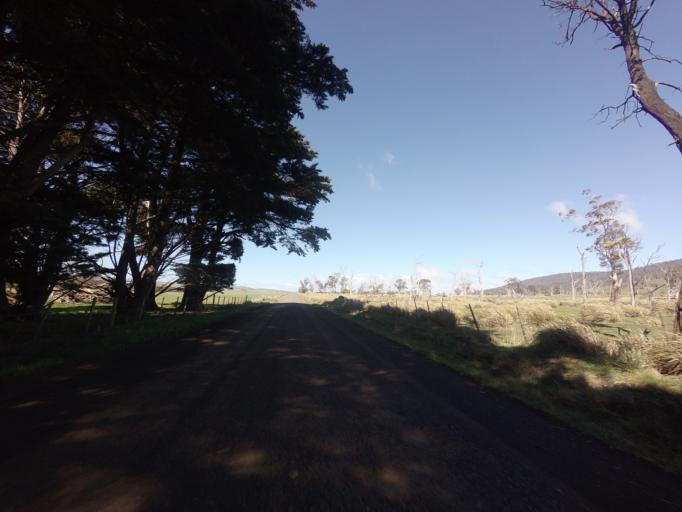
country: AU
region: Tasmania
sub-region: Northern Midlands
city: Evandale
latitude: -41.9445
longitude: 147.4294
